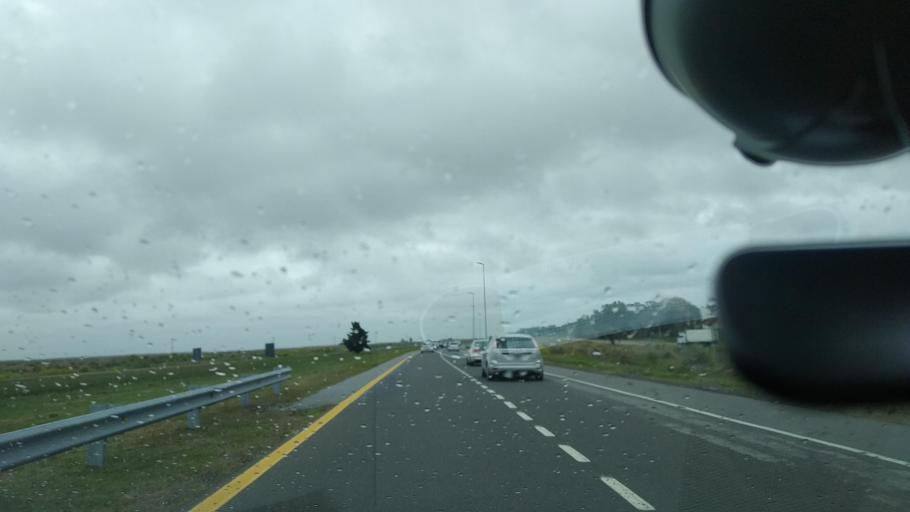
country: AR
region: Buenos Aires
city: San Clemente del Tuyu
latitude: -36.3895
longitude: -56.7439
